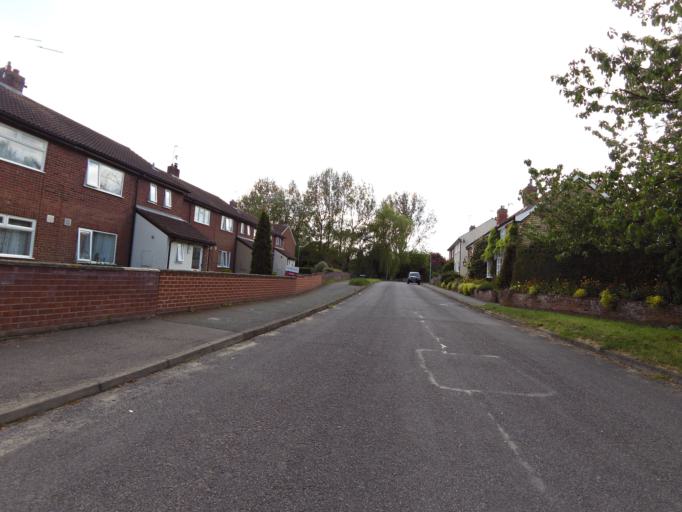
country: GB
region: England
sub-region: Suffolk
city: Beccles
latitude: 52.4468
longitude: 1.6315
